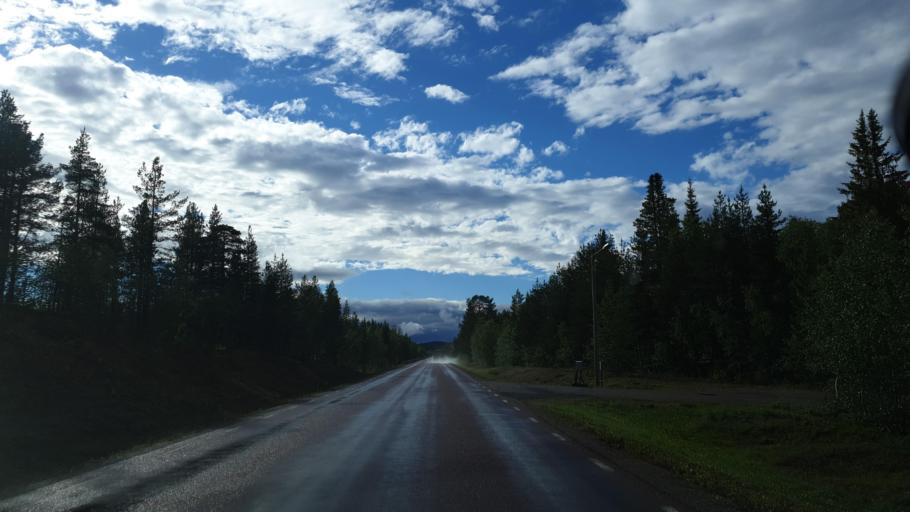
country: SE
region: Norrbotten
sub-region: Arjeplogs Kommun
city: Arjeplog
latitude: 66.0062
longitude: 18.1075
